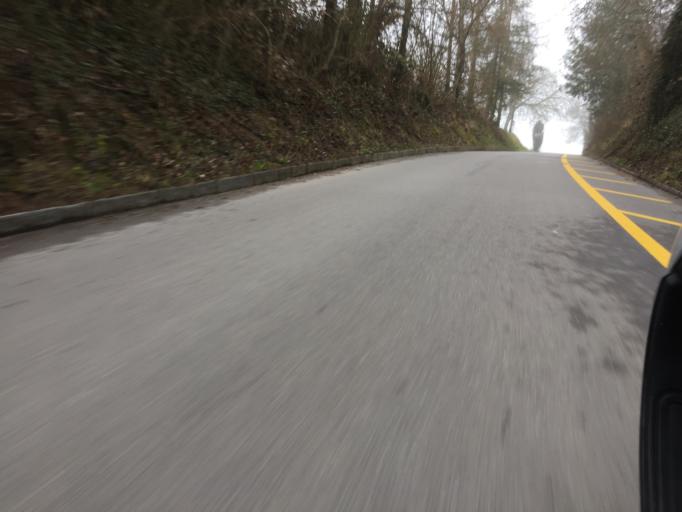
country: CH
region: Bern
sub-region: Seeland District
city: Grossaffoltern
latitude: 47.0996
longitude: 7.3635
